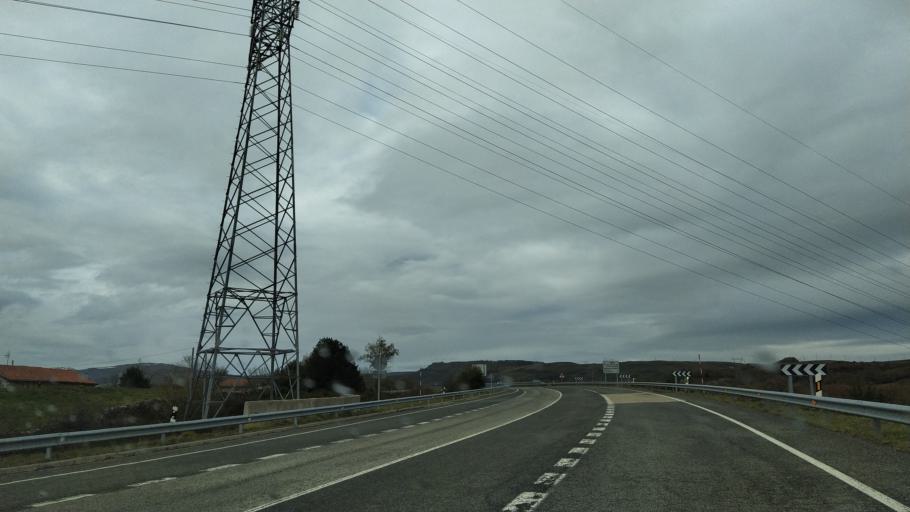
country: ES
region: Castille and Leon
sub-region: Provincia de Burgos
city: Arija
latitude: 43.0057
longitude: -3.8423
